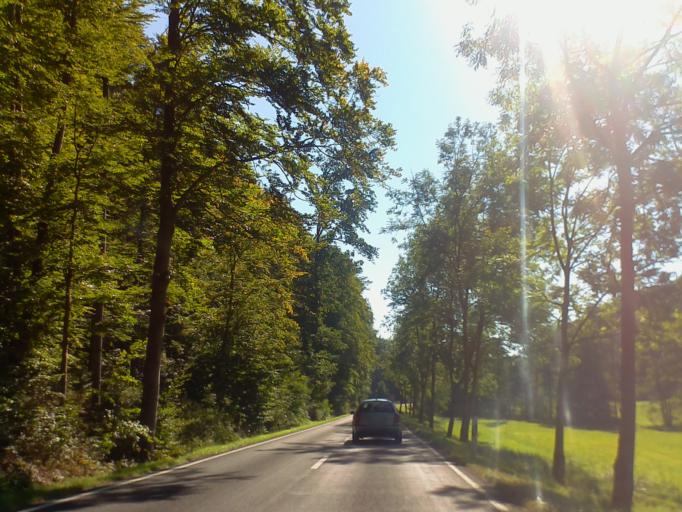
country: DE
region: Thuringia
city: Geisenhain
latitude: 50.8189
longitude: 11.7132
